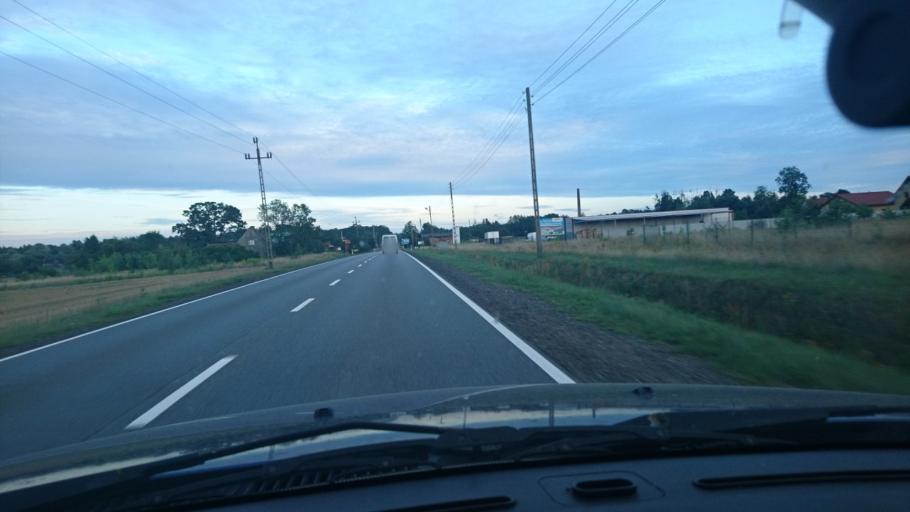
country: PL
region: Silesian Voivodeship
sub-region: Powiat tarnogorski
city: Tworog
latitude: 50.5186
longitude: 18.7287
